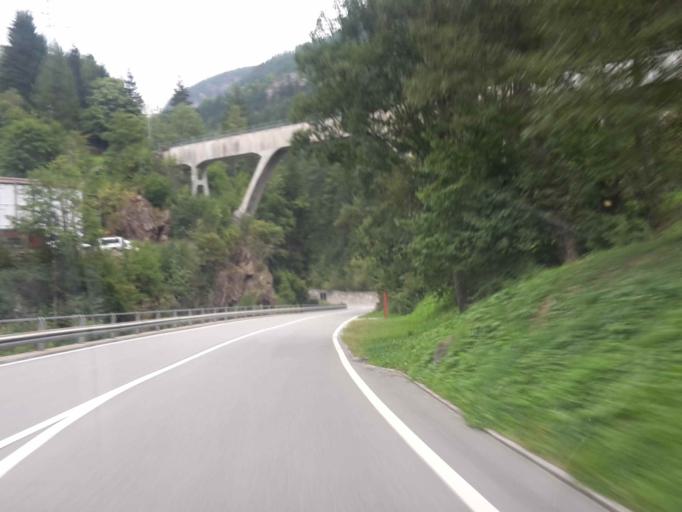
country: CH
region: Valais
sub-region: Saint-Maurice District
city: Salvan
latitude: 46.0585
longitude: 6.9590
